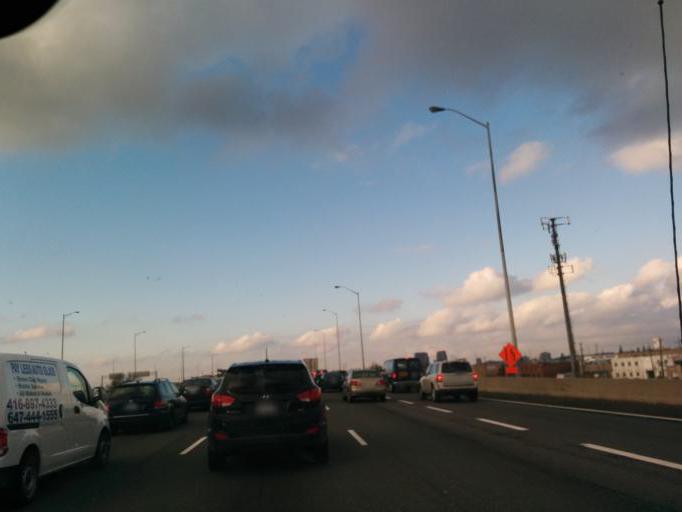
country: CA
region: Ontario
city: Etobicoke
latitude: 43.7006
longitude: -79.6093
